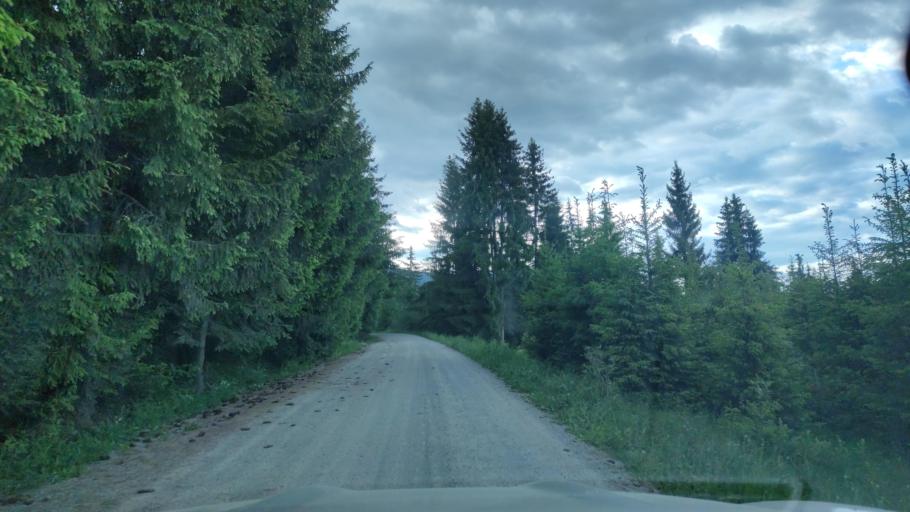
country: RO
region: Harghita
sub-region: Comuna Joseni
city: Joseni
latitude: 46.6663
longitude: 25.3823
